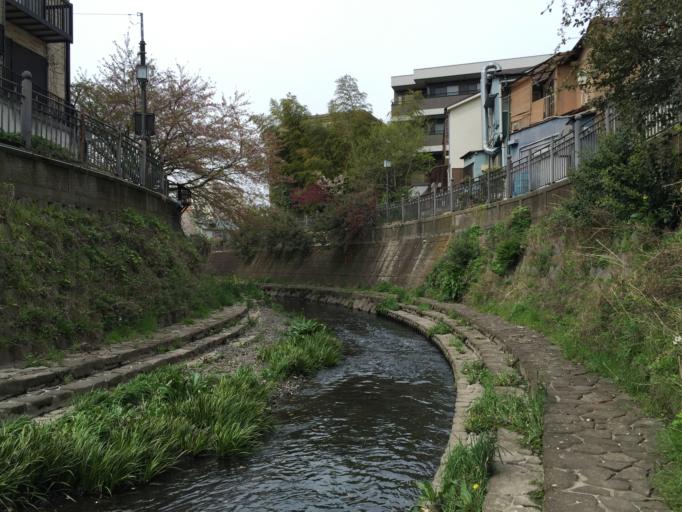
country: JP
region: Kanagawa
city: Yokohama
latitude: 35.4075
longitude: 139.5941
